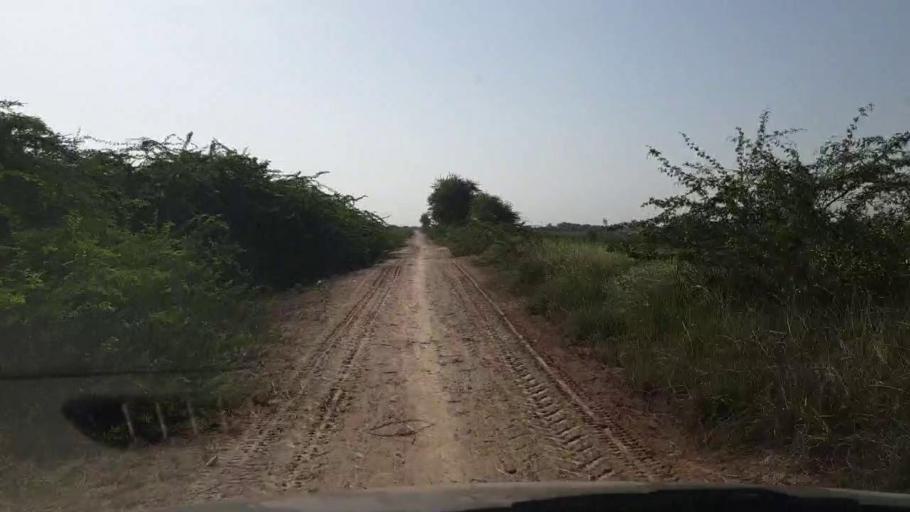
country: PK
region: Sindh
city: Kadhan
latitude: 24.5978
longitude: 69.0752
